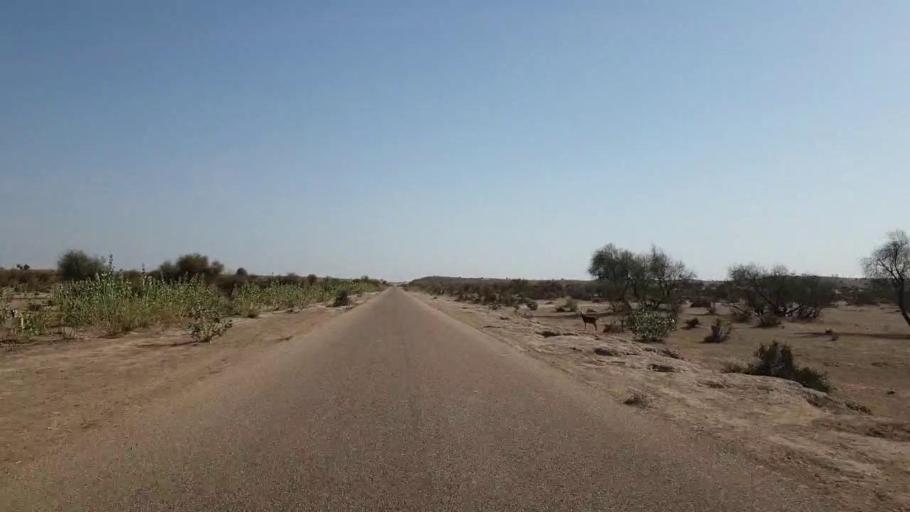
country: PK
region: Sindh
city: Nabisar
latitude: 25.0939
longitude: 70.0395
